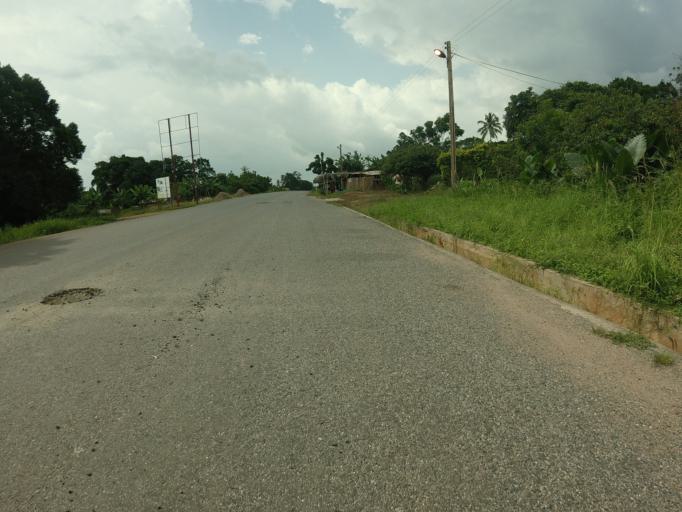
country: GH
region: Volta
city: Kpandu
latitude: 6.8835
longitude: 0.4213
